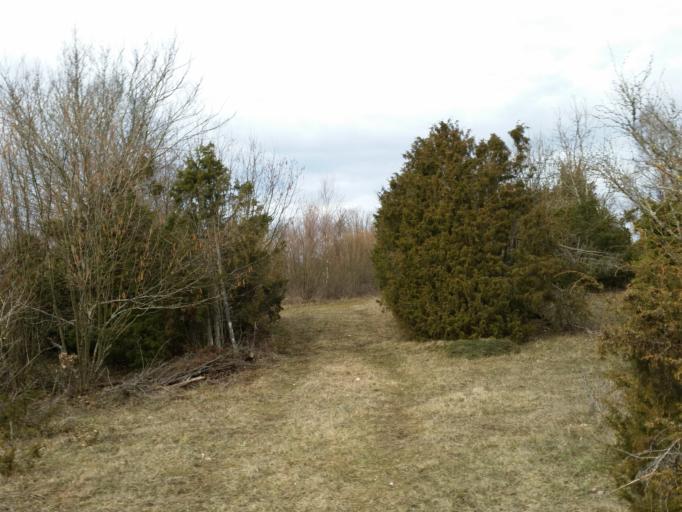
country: SE
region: Kalmar
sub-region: Morbylanga Kommun
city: Sodra Sandby
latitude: 56.6777
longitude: 16.5808
